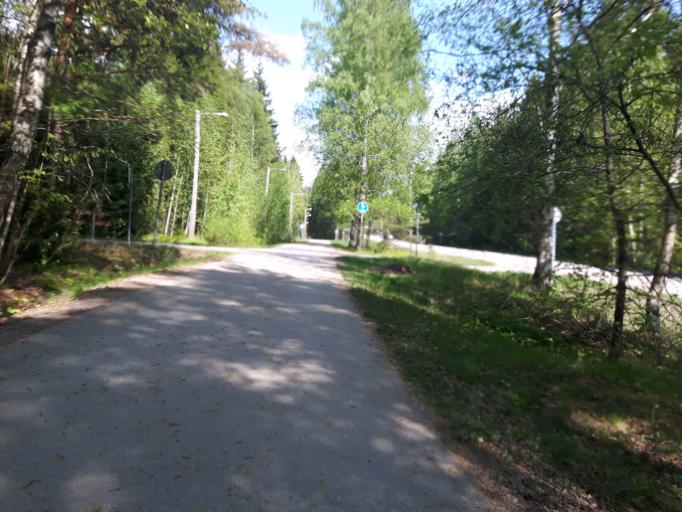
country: FI
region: Uusimaa
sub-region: Porvoo
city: Porvoo
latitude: 60.3869
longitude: 25.6292
